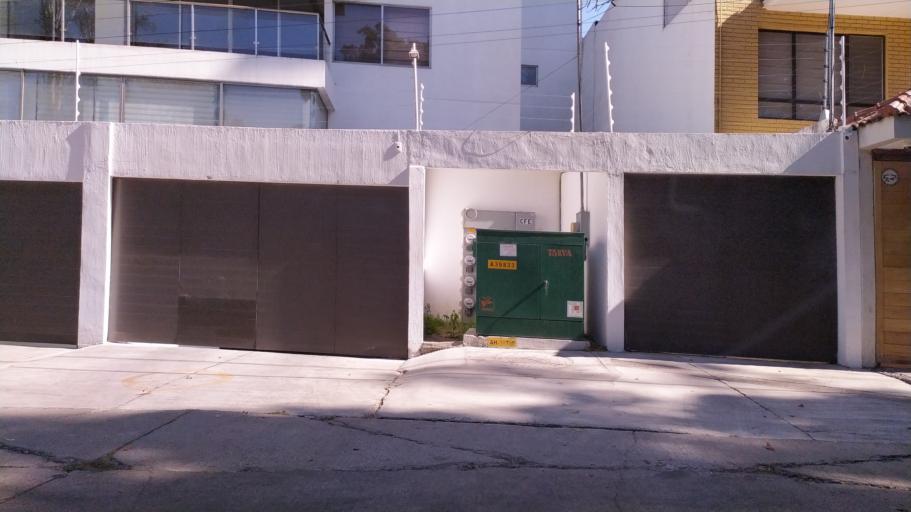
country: MX
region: Jalisco
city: Guadalajara
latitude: 20.6920
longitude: -103.3897
